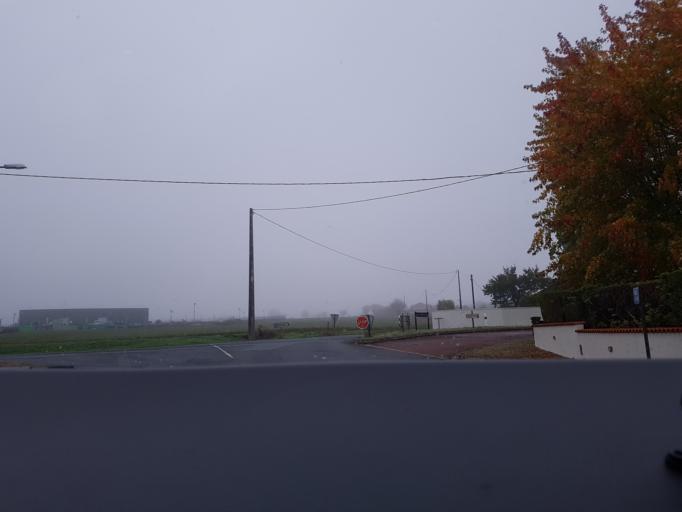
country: FR
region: Poitou-Charentes
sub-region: Departement des Deux-Sevres
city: Exireuil
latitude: 46.4285
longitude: -0.2024
